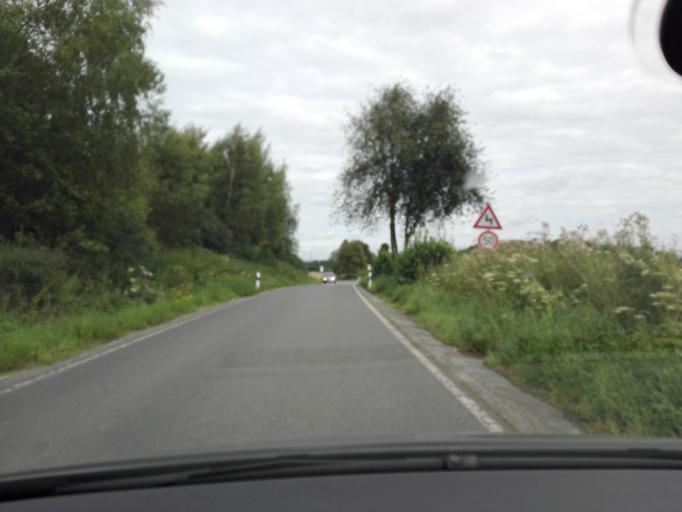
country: DE
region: North Rhine-Westphalia
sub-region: Regierungsbezirk Arnsberg
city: Unna
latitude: 51.5134
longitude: 7.7293
